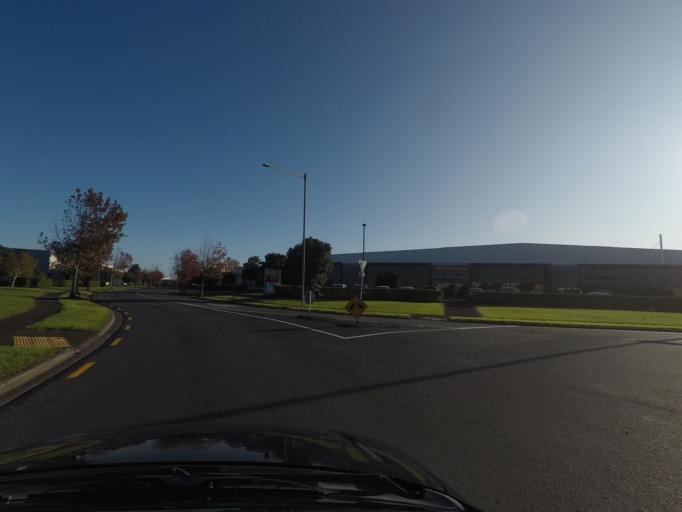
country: NZ
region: Auckland
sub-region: Auckland
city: Manukau City
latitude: -36.9407
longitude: 174.8784
